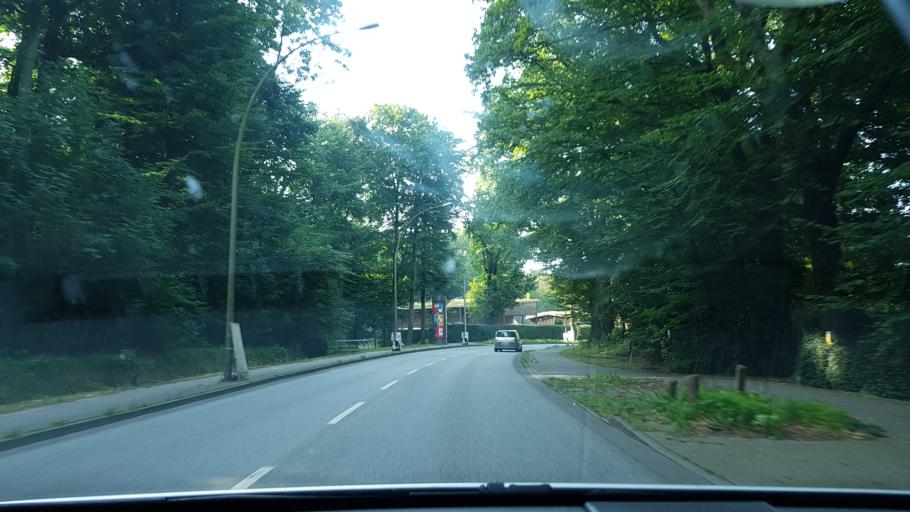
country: DE
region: Hamburg
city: Bergstedt
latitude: 53.6426
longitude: 10.1582
